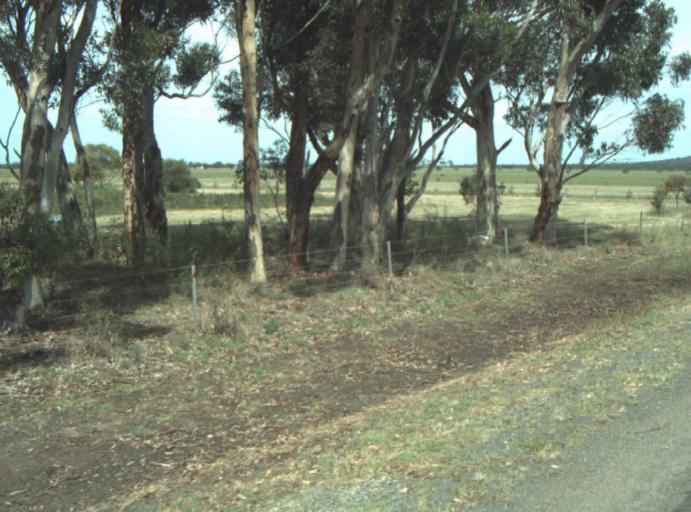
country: AU
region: Victoria
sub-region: Wyndham
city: Little River
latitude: -37.9588
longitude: 144.4793
